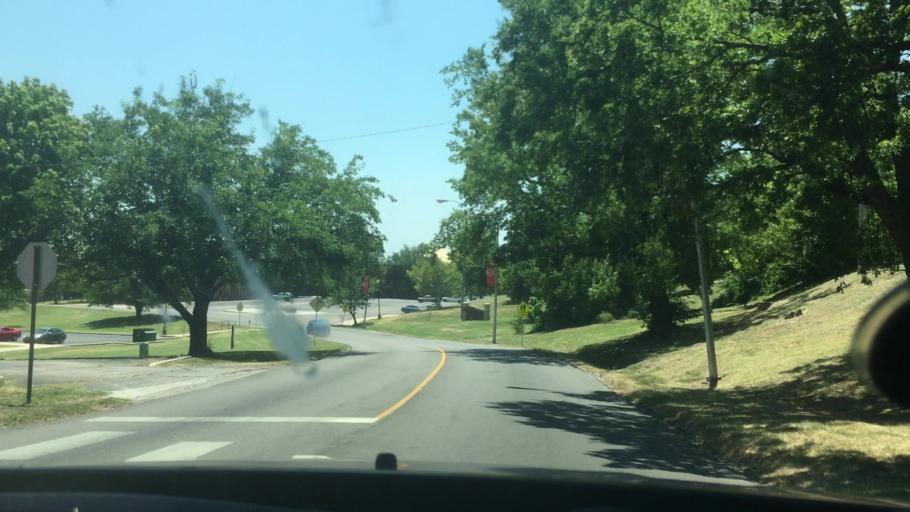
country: US
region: Oklahoma
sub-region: Pontotoc County
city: Ada
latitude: 34.7756
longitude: -96.6633
